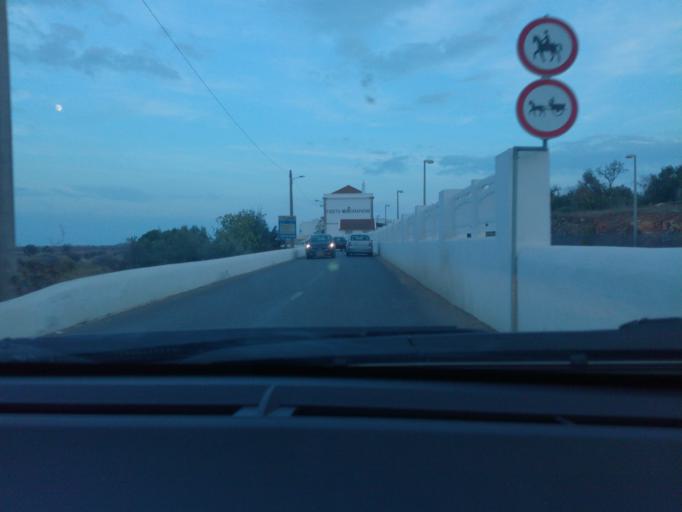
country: PT
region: Faro
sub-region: Olhao
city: Laranjeiro
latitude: 37.0608
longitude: -7.7525
